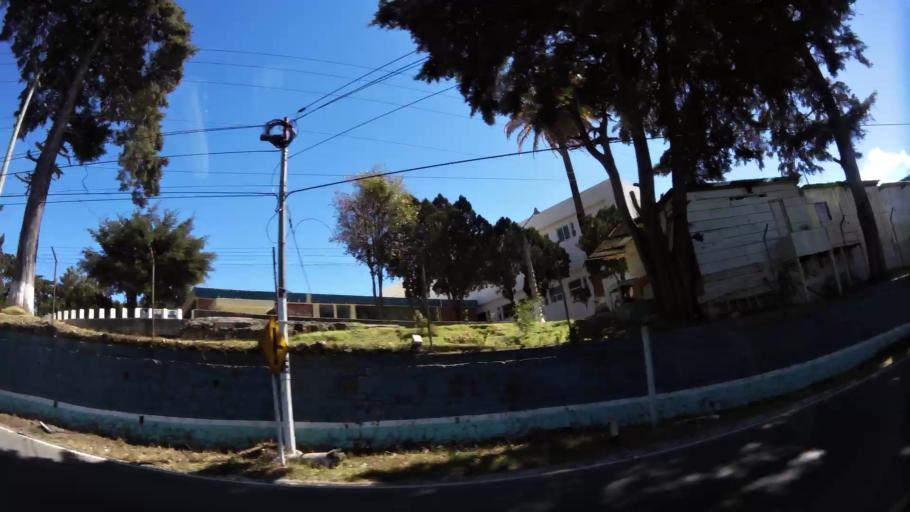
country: GT
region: Solola
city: Solola
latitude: 14.7646
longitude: -91.1771
